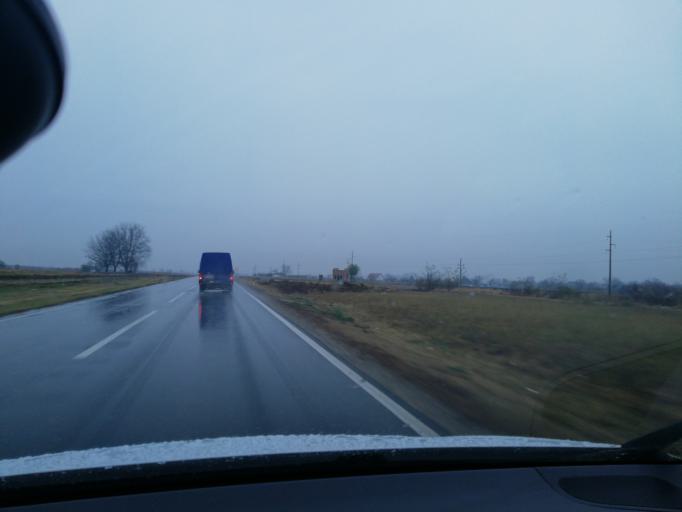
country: RS
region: Autonomna Pokrajina Vojvodina
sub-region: Sremski Okrug
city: Ruma
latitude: 45.0190
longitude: 19.8399
